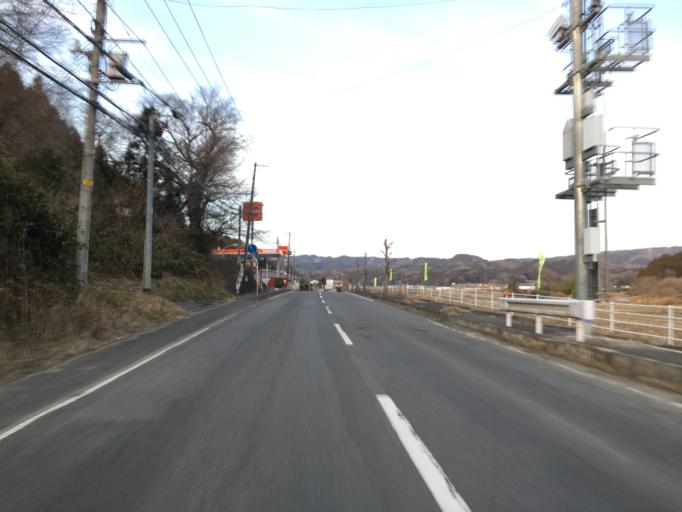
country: JP
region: Ibaraki
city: Daigo
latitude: 36.8579
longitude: 140.4111
